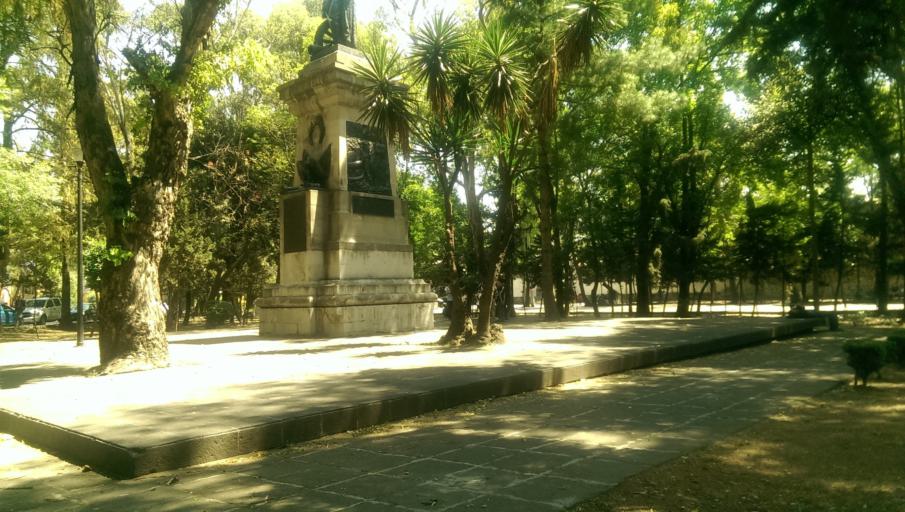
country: MX
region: Mexico City
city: Coyoacan
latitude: 19.3549
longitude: -99.1495
